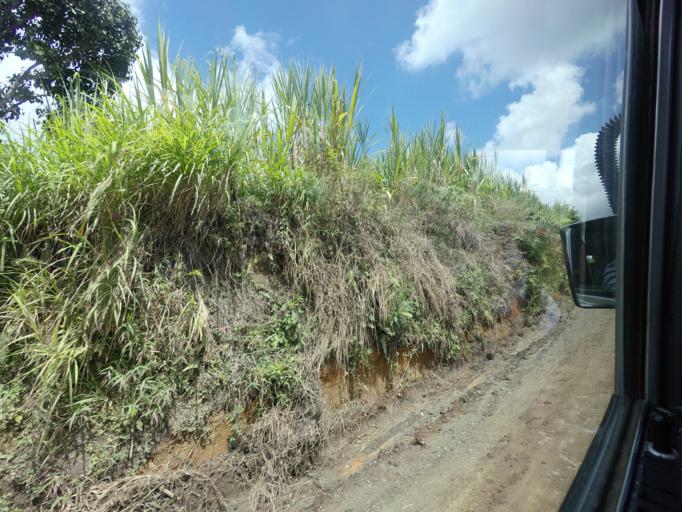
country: CO
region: Huila
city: Isnos
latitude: 1.9415
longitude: -76.2687
